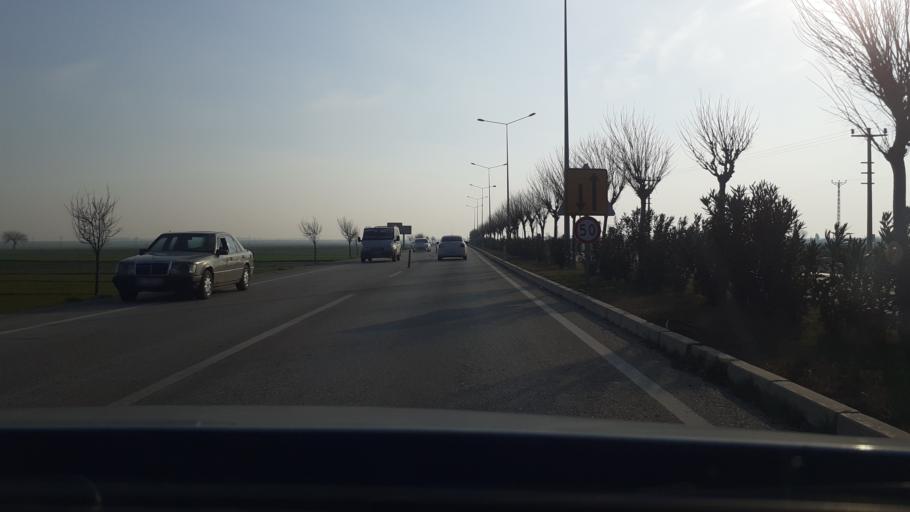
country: TR
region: Hatay
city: Serinyol
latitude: 36.3712
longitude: 36.2458
